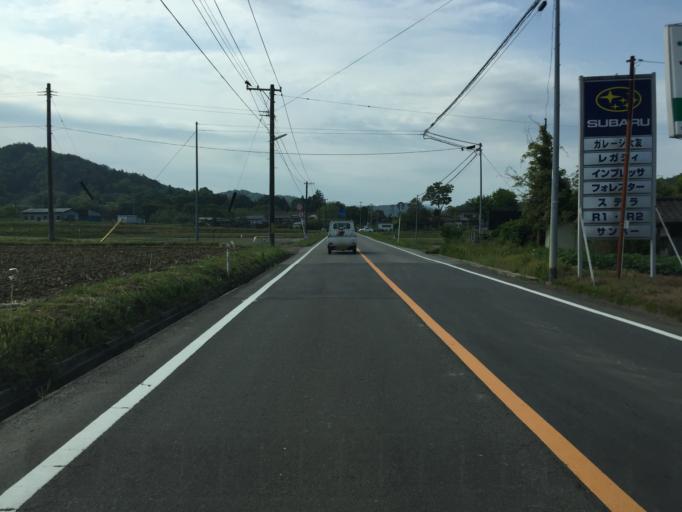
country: JP
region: Fukushima
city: Yanagawamachi-saiwaicho
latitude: 37.8084
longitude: 140.6194
